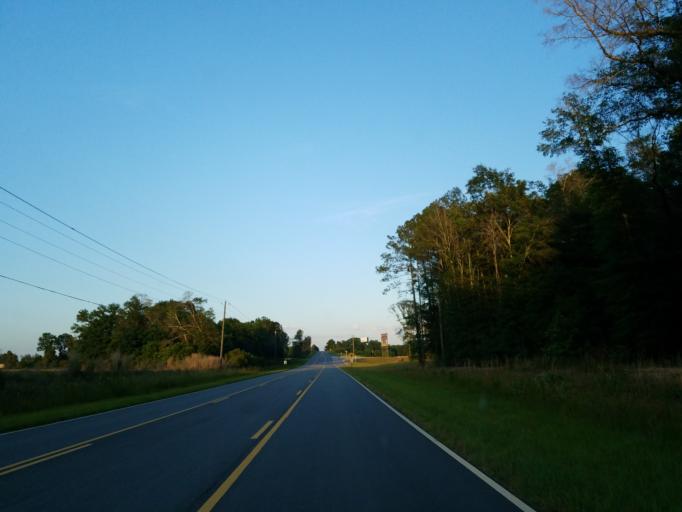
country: US
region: Georgia
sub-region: Crisp County
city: Cordele
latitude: 31.9257
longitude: -83.7499
